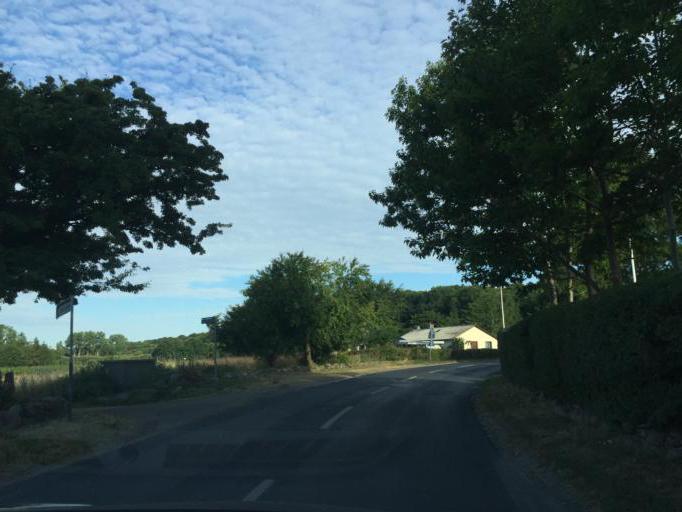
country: DK
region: South Denmark
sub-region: Assens Kommune
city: Harby
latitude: 55.1487
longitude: 10.0196
